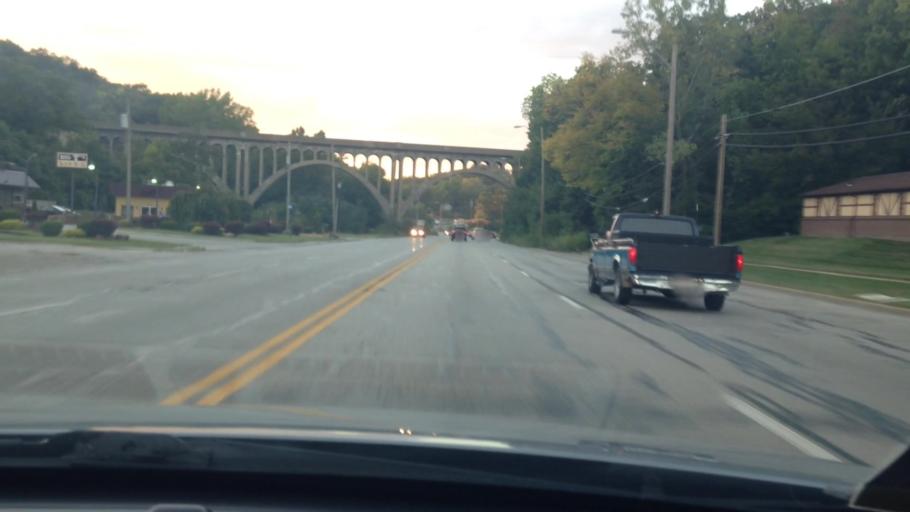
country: US
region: Missouri
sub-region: Jackson County
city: Raytown
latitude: 39.0321
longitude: -94.5126
